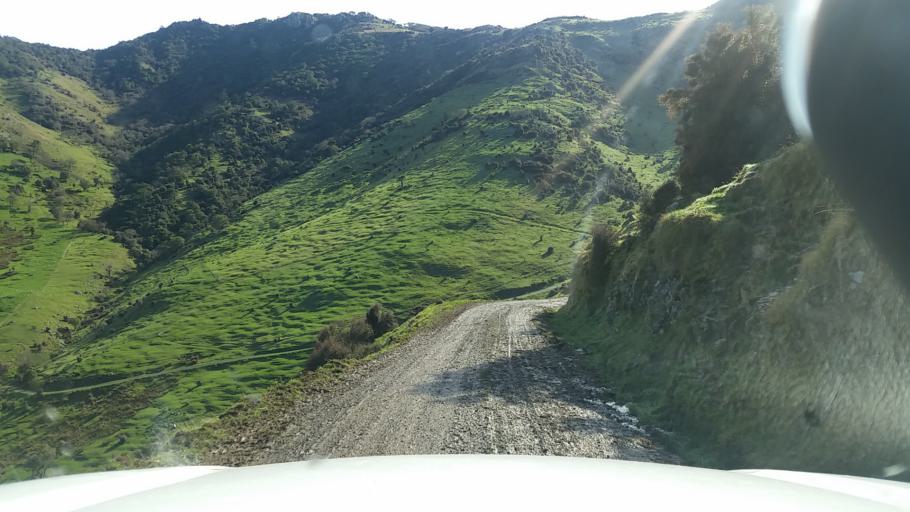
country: NZ
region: Canterbury
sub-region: Christchurch City
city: Christchurch
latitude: -43.6670
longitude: 172.8746
